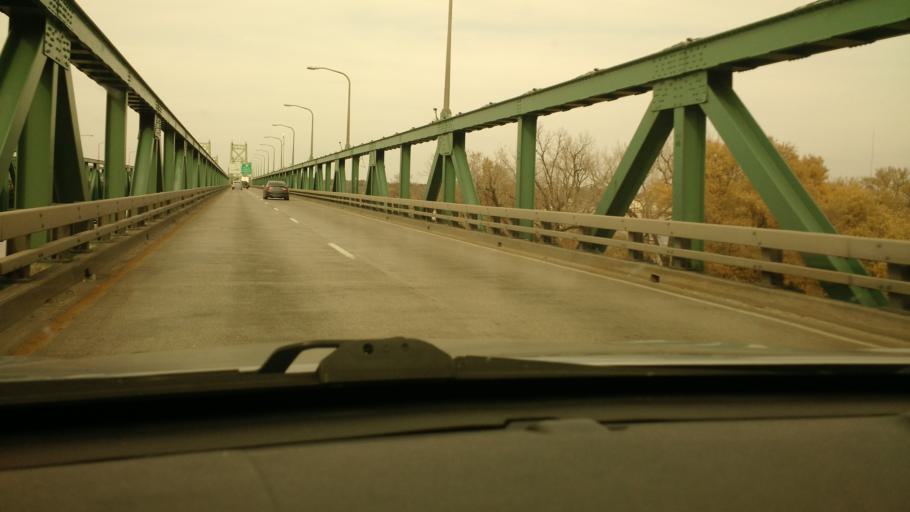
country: US
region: Illinois
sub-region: Rock Island County
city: Moline
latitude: 41.5139
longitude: -90.5128
